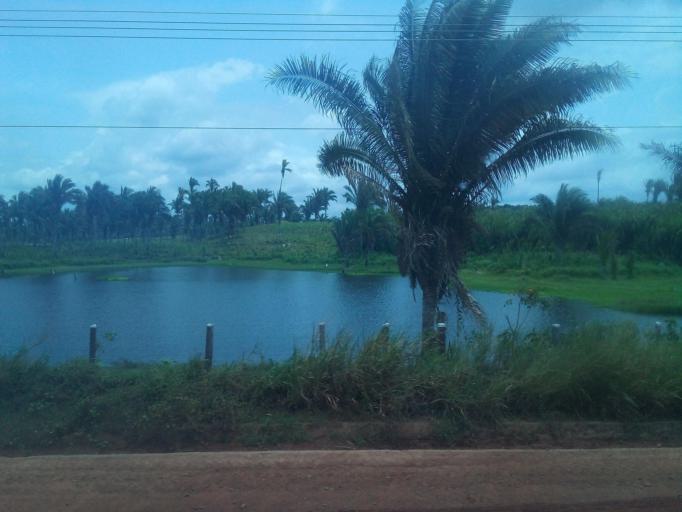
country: BR
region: Maranhao
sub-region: Santa Ines
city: Santa Ines
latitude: -3.6955
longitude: -45.6209
